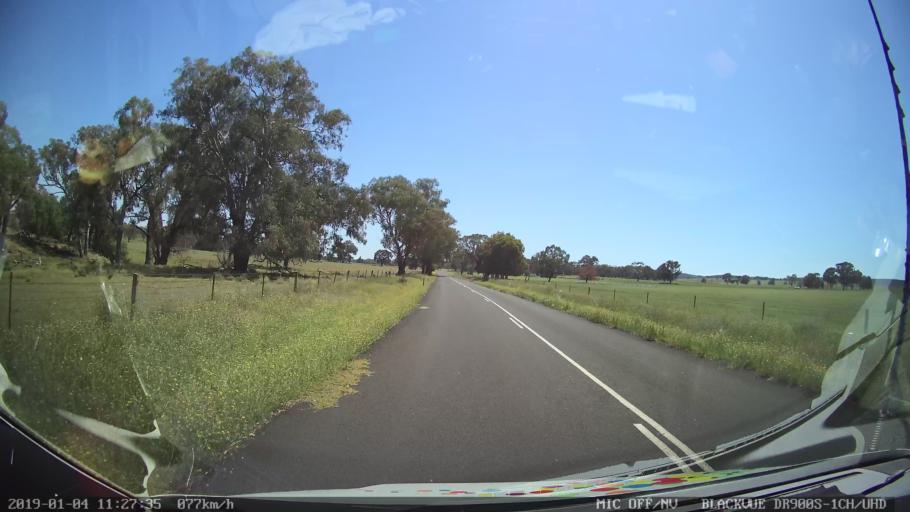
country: AU
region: New South Wales
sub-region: Cabonne
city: Molong
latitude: -33.1081
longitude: 148.7644
